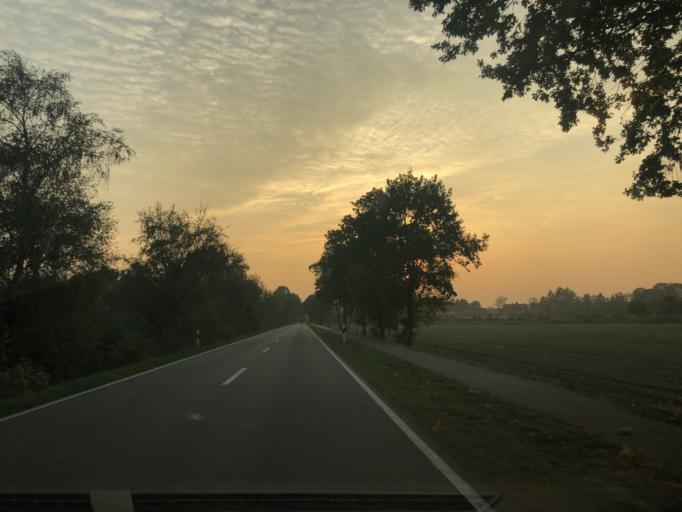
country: DE
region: Lower Saxony
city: Garrel
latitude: 53.0243
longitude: 8.0733
